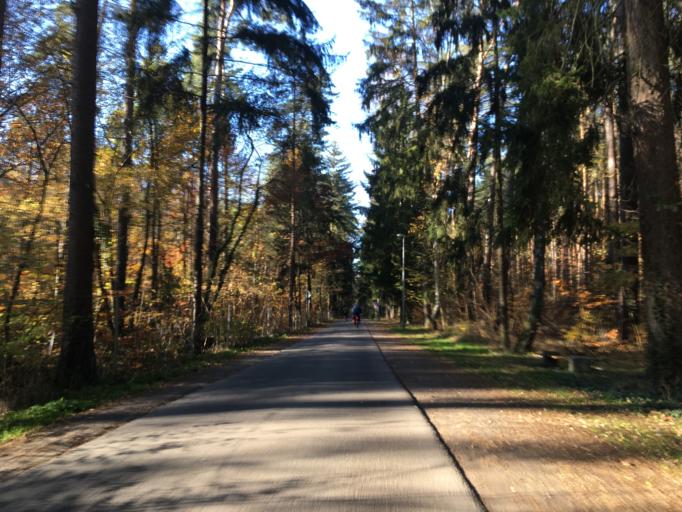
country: DE
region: Brandenburg
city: Bad Saarow
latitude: 52.2935
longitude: 14.0418
